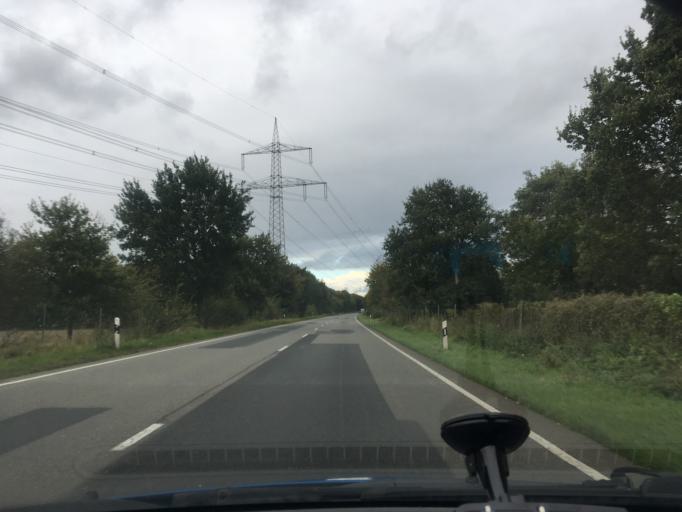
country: DE
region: Lower Saxony
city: Handorf
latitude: 53.3478
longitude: 10.3371
